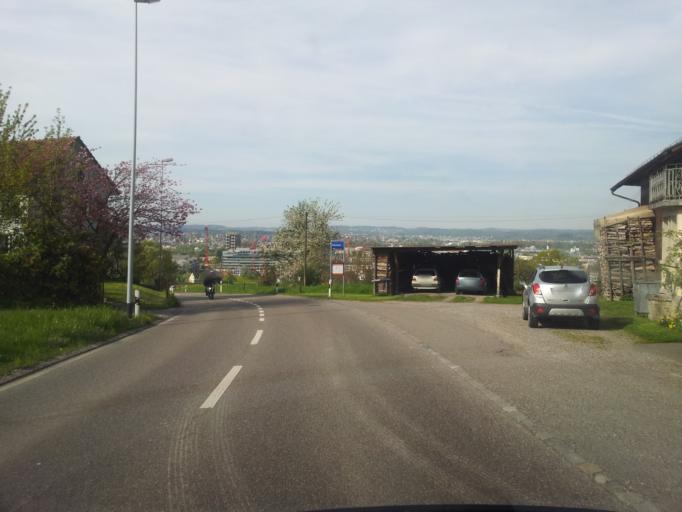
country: CH
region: Zurich
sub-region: Bezirk Uster
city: Gockhausen
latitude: 47.3892
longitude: 8.5965
